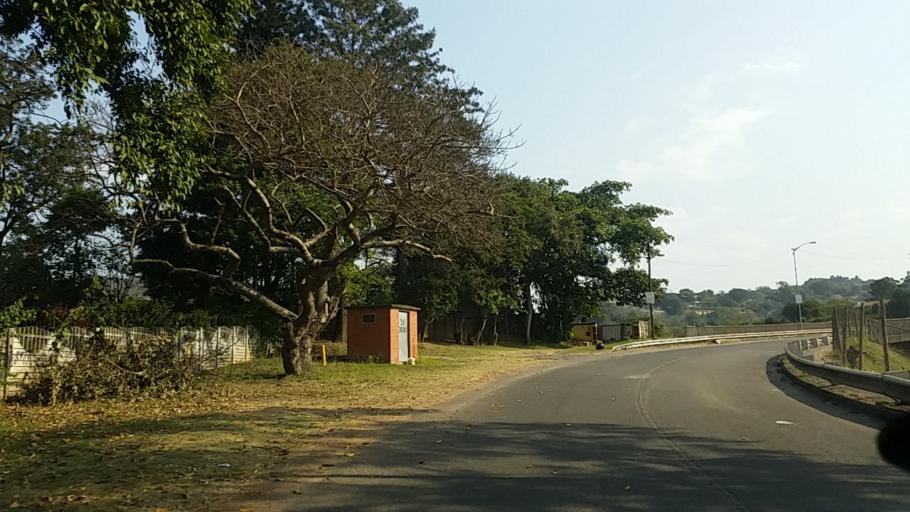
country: ZA
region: KwaZulu-Natal
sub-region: eThekwini Metropolitan Municipality
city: Berea
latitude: -29.8451
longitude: 30.9419
